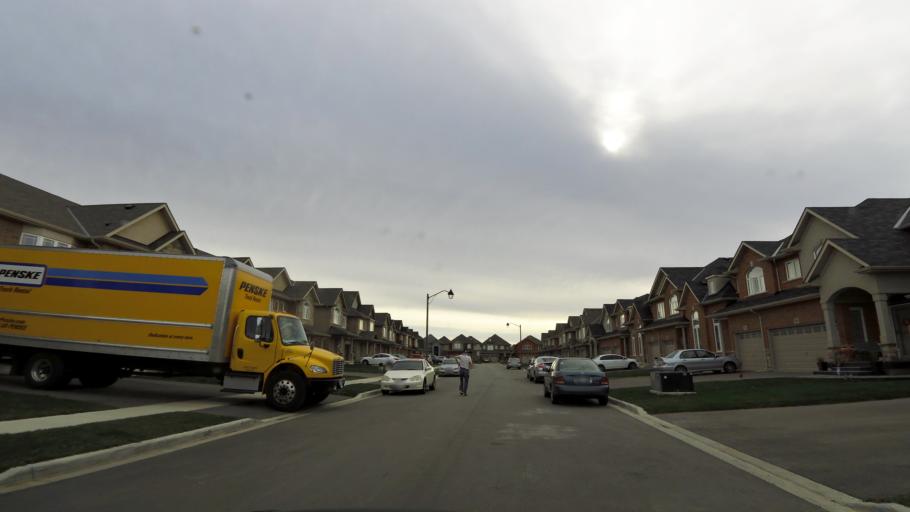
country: CA
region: Ontario
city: Hamilton
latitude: 43.1778
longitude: -79.7993
